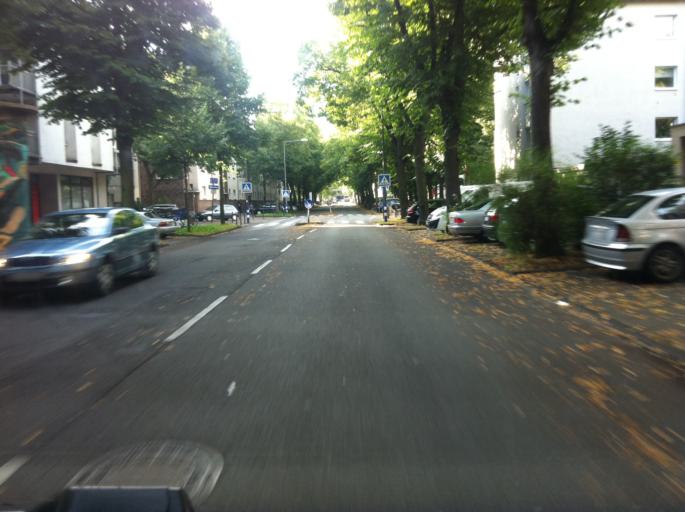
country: DE
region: North Rhine-Westphalia
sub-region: Regierungsbezirk Koln
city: Bilderstoeckchen
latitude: 50.9553
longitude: 6.9038
